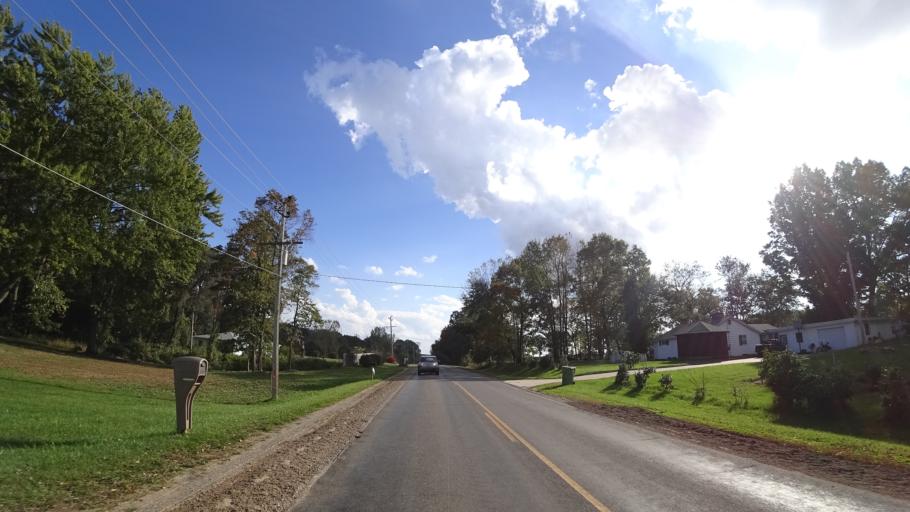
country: US
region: Michigan
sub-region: Saint Joseph County
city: Centreville
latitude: 41.9511
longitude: -85.5278
